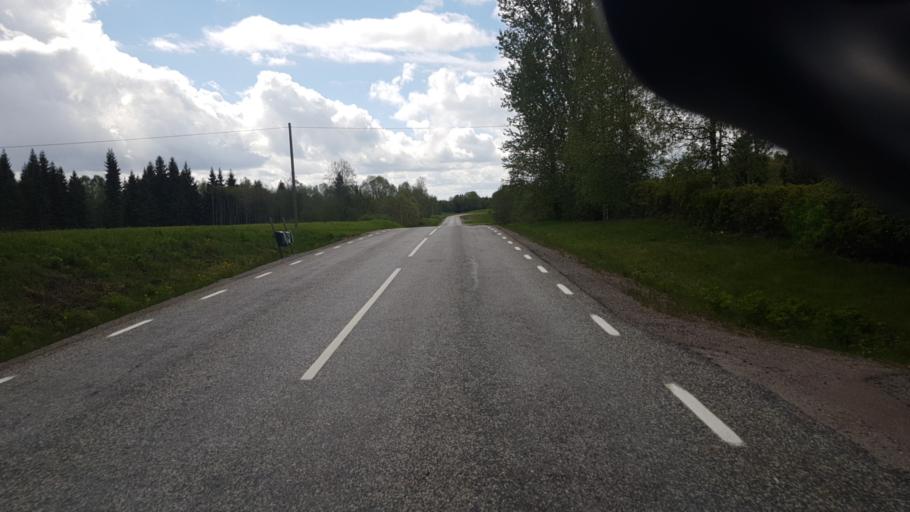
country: SE
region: Vaermland
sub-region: Arjangs Kommun
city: Arjaeng
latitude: 59.5644
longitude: 12.1220
